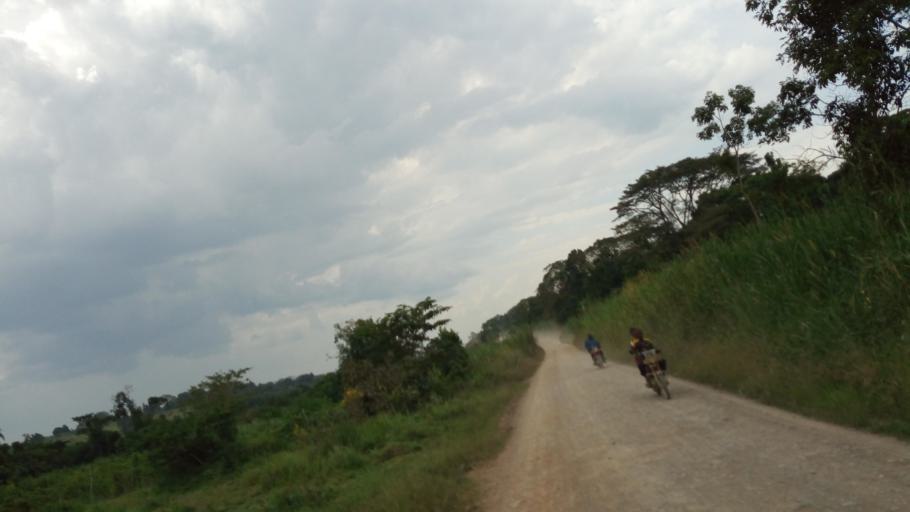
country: UG
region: Central Region
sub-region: Kiboga District
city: Kiboga
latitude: 0.7144
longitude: 31.7501
